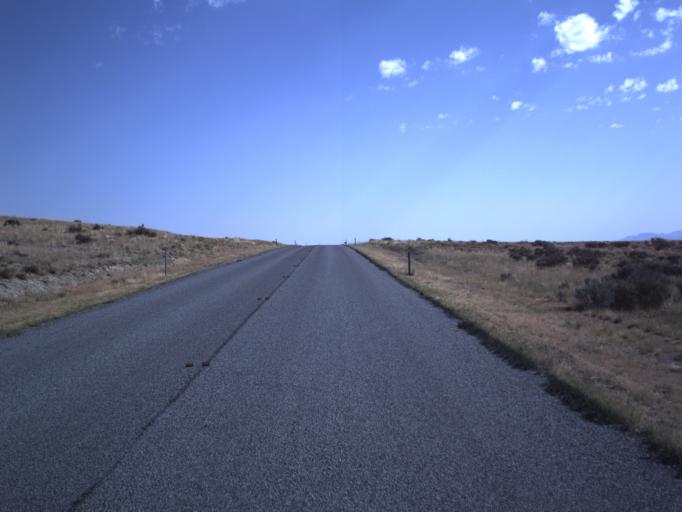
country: US
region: Utah
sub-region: Millard County
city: Fillmore
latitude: 38.9070
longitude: -112.8186
